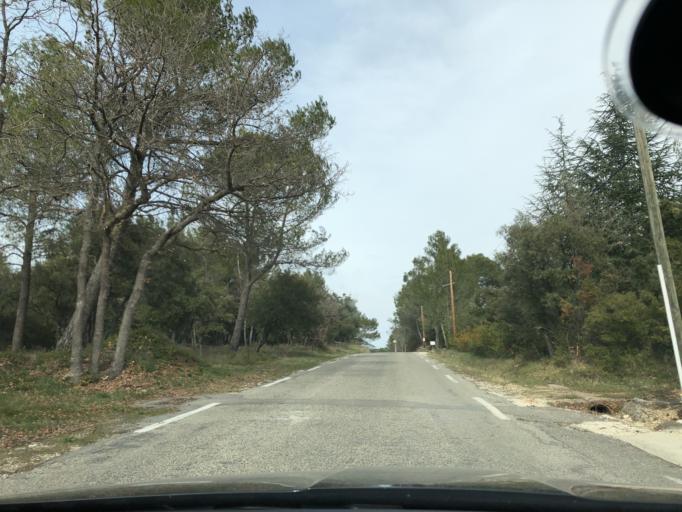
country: FR
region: Provence-Alpes-Cote d'Azur
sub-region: Departement du Vaucluse
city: Menerbes
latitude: 43.8428
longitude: 5.2183
